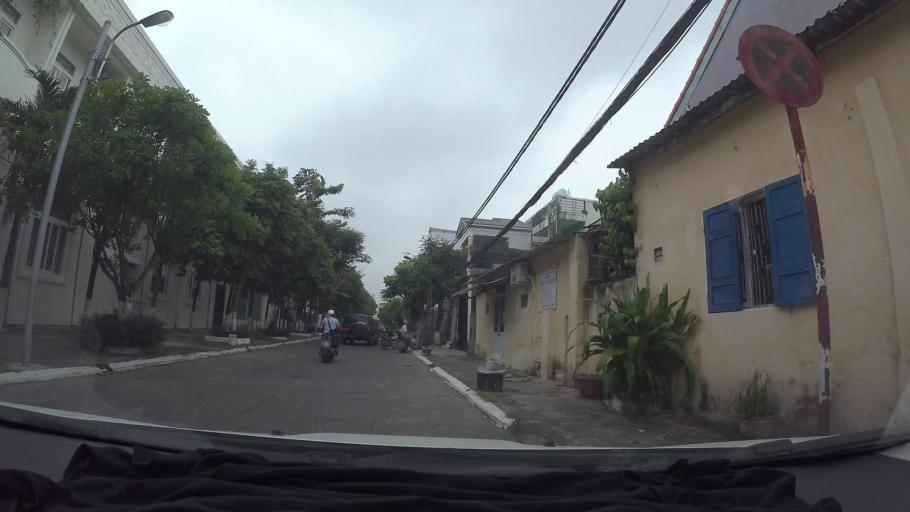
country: VN
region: Da Nang
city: Da Nang
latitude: 16.0518
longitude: 108.2112
